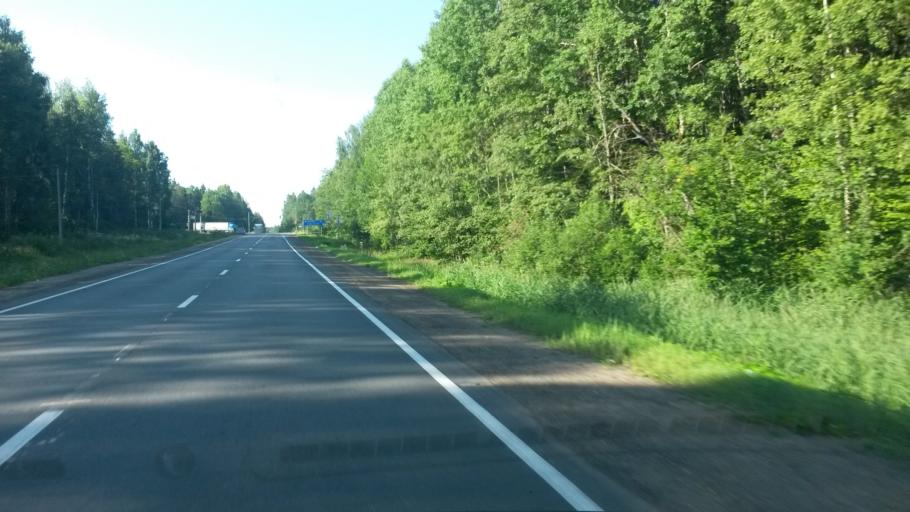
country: RU
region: Jaroslavl
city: Gavrilov-Yam
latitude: 57.2751
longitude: 39.9506
